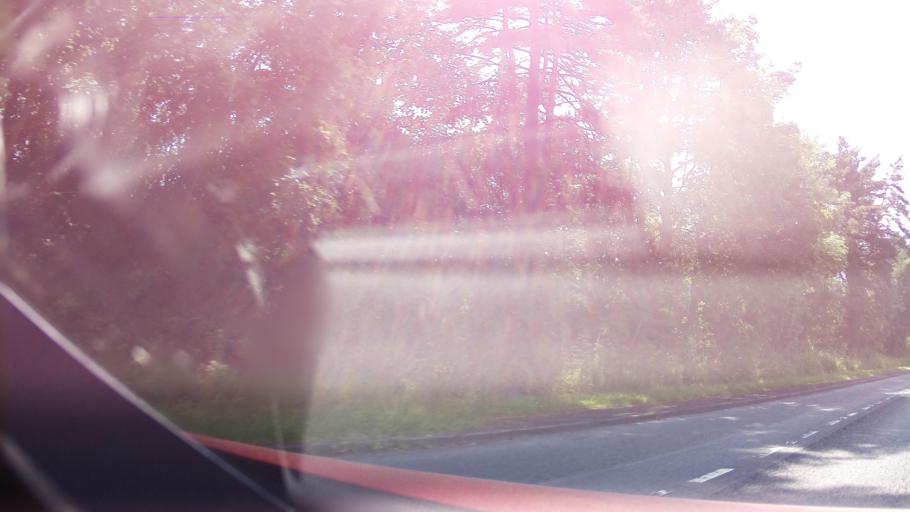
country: GB
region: England
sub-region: Worcestershire
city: Bromsgrove
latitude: 52.3305
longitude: -2.0282
